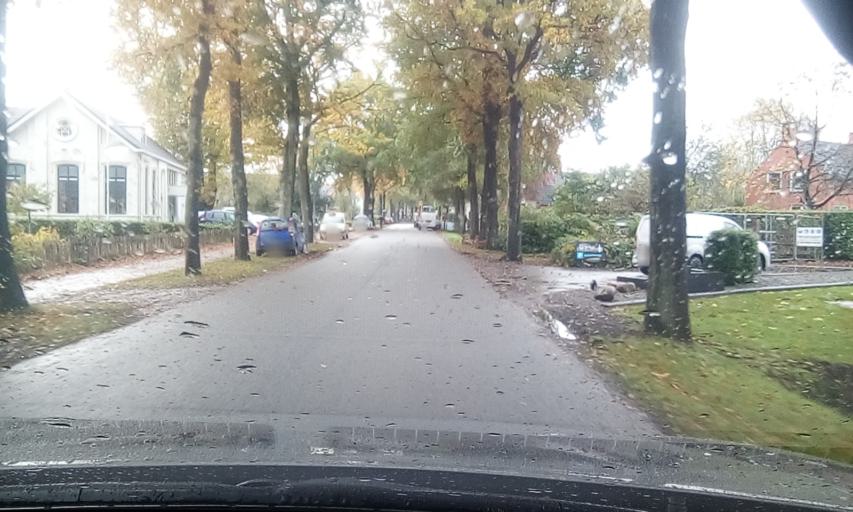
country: NL
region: Groningen
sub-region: Gemeente Hoogezand-Sappemeer
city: Hoogezand
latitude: 53.2056
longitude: 6.7070
